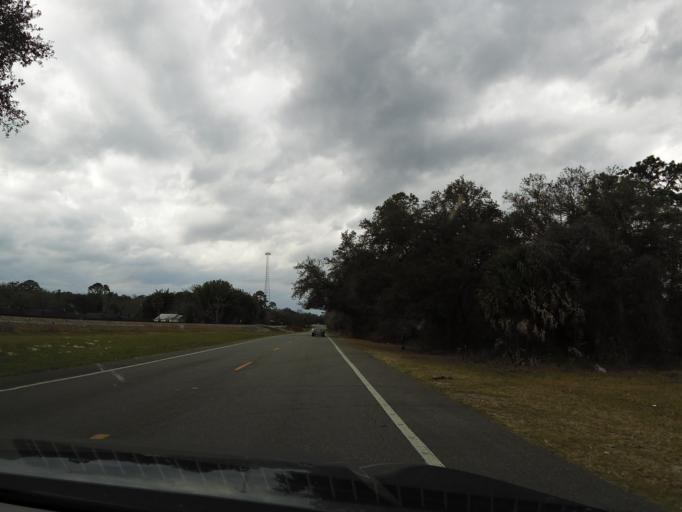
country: US
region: Florida
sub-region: Putnam County
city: Crescent City
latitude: 29.3598
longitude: -81.5056
